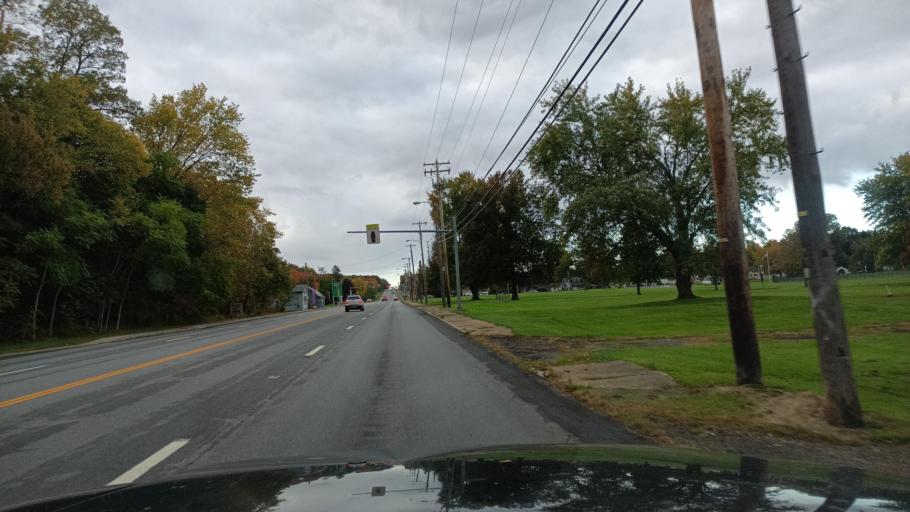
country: US
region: Ohio
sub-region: Trumbull County
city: Lordstown
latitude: 41.1685
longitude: -80.8574
